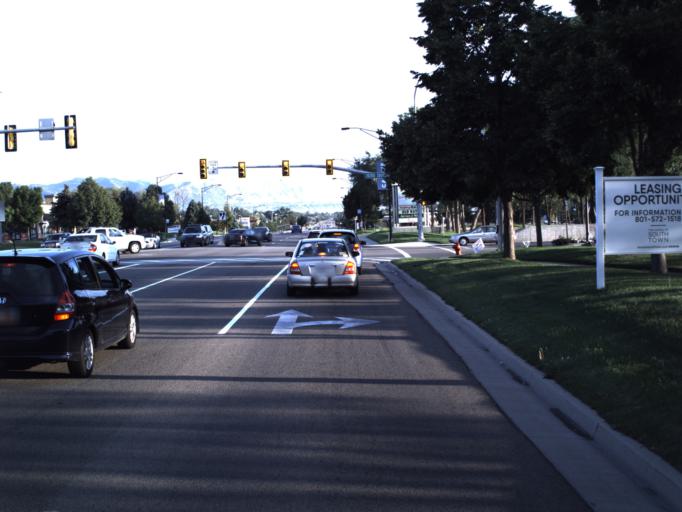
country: US
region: Utah
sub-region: Salt Lake County
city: Sandy City
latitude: 40.5665
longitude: -111.8910
